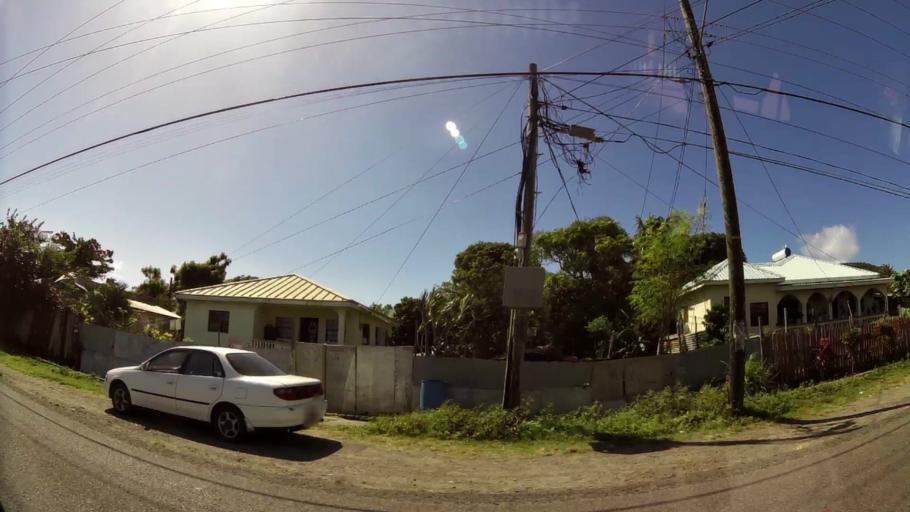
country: LC
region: Laborie Quarter
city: Laborie
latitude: 13.7446
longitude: -60.9575
